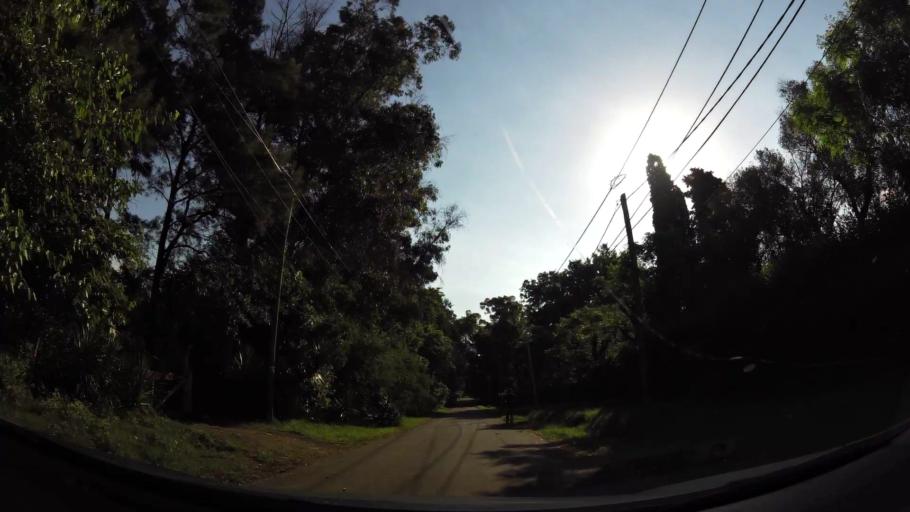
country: AR
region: Buenos Aires
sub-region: Partido de Tigre
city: Tigre
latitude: -34.4710
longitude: -58.6325
